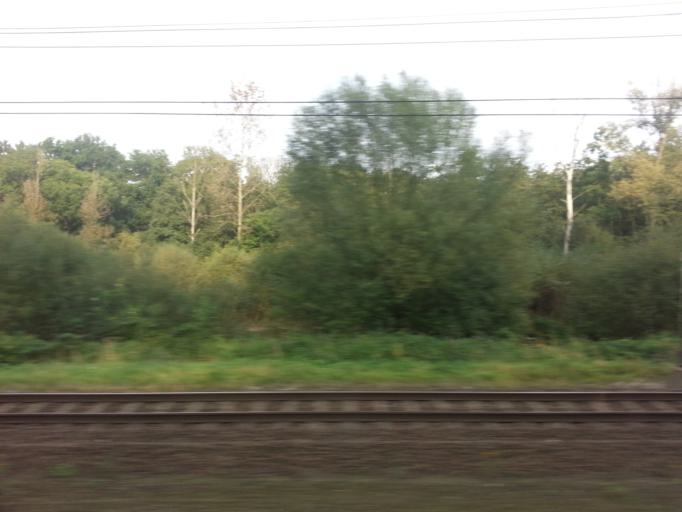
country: NL
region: North Brabant
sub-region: Gemeente Boxtel
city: Boxtel
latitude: 51.5514
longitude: 5.3511
